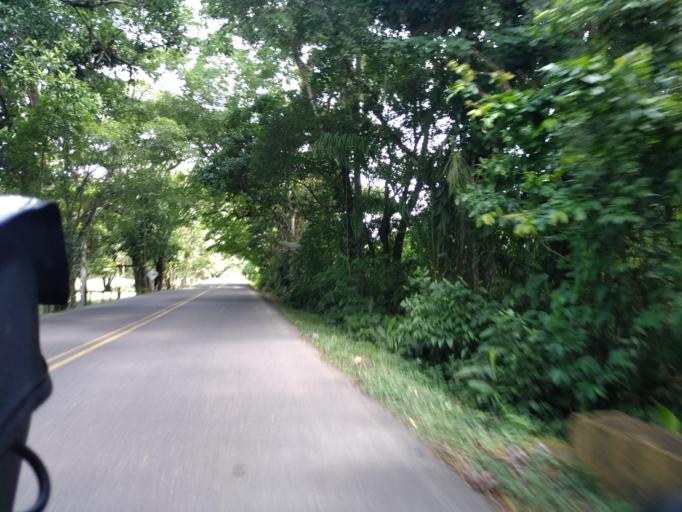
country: CO
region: Santander
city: Puerto Parra
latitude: 6.5195
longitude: -74.0768
